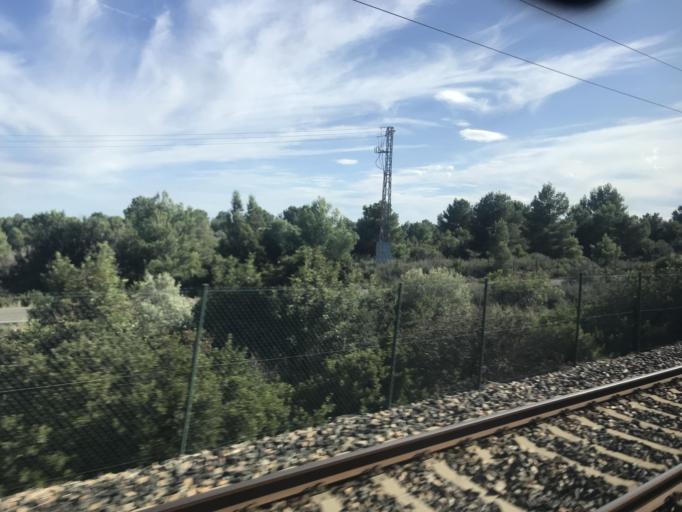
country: ES
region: Catalonia
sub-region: Provincia de Tarragona
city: l'Ametlla de Mar
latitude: 40.8729
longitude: 0.7861
